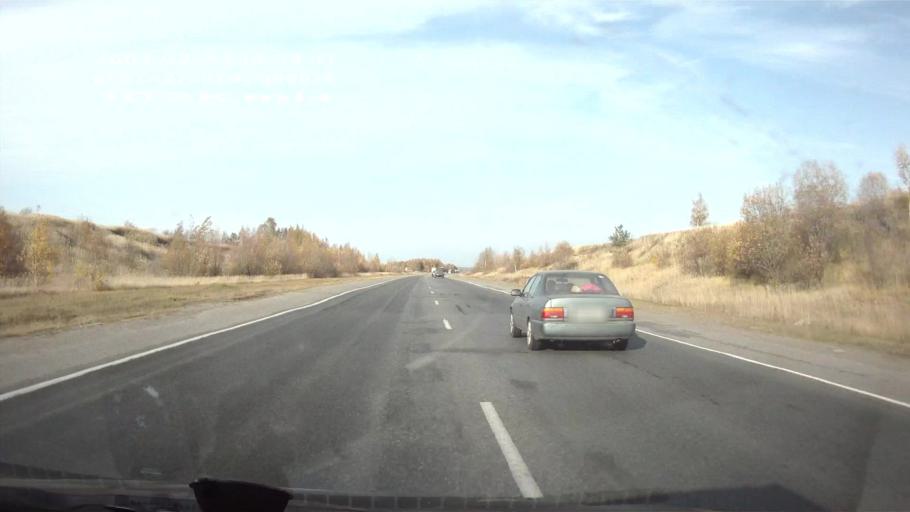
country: RU
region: Chuvashia
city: Kugesi
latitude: 56.0424
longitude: 47.3667
